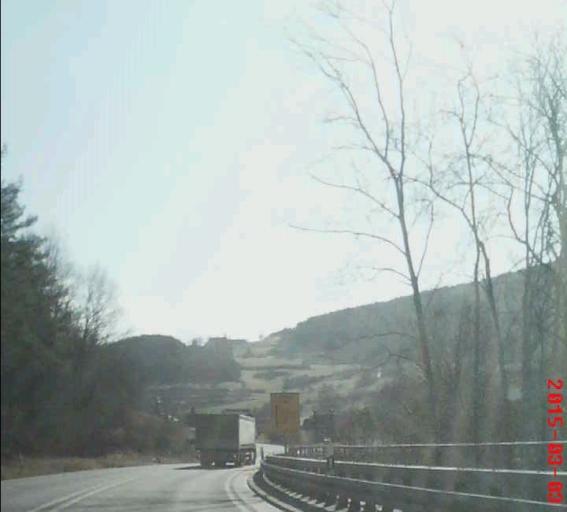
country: DE
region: Thuringia
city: Bad Blankenburg
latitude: 50.7235
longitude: 11.2658
